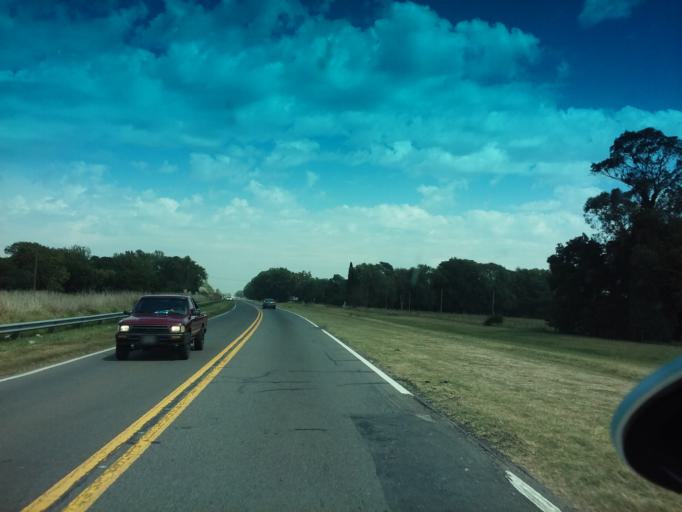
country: AR
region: Buenos Aires
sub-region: Partido de Carlos Casares
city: Carlos Casares
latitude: -35.6268
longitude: -61.3310
